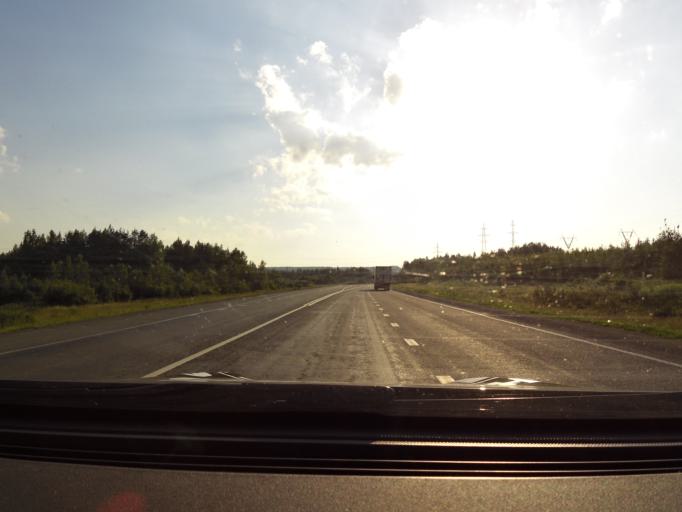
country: RU
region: Sverdlovsk
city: Revda
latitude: 56.8264
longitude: 59.8839
